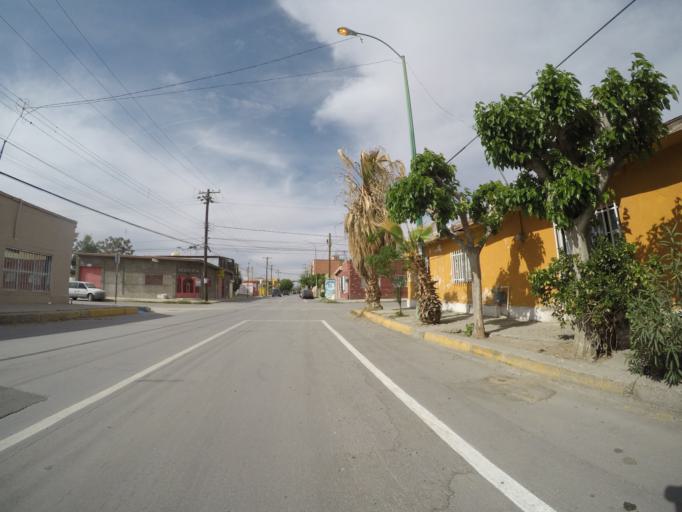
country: MX
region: Chihuahua
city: Ciudad Juarez
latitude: 31.7422
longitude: -106.4639
